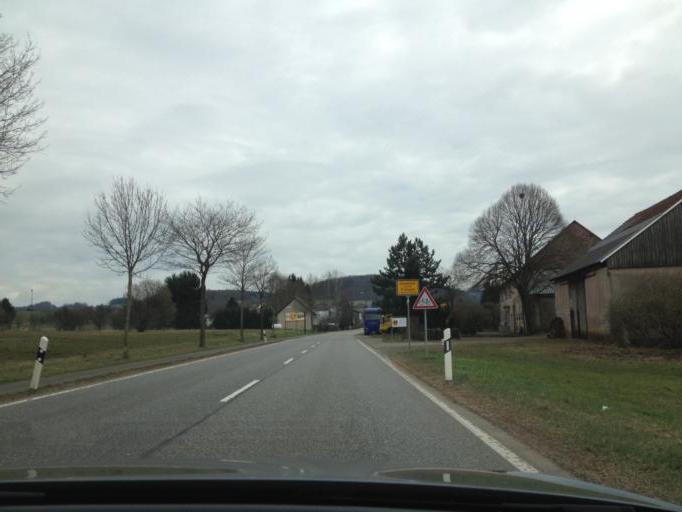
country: DE
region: Rheinland-Pfalz
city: Hahnweiler
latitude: 49.5523
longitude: 7.1874
